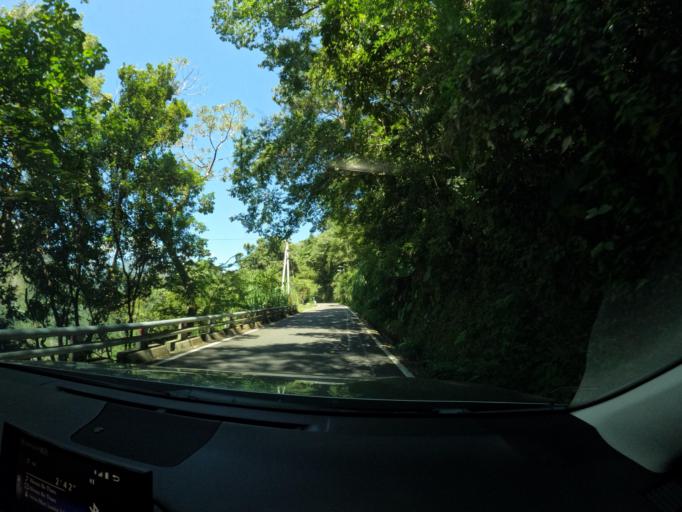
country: TW
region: Taiwan
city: Yujing
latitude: 23.2624
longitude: 120.8497
